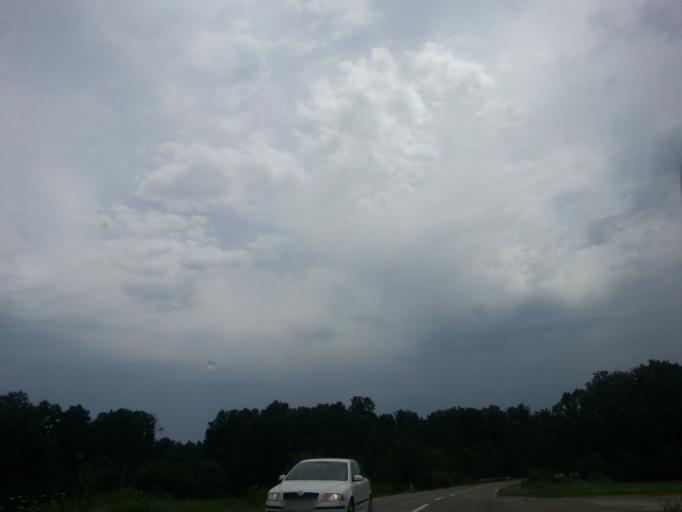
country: BA
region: Republika Srpska
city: Velika Obarska
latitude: 44.7990
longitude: 19.0836
